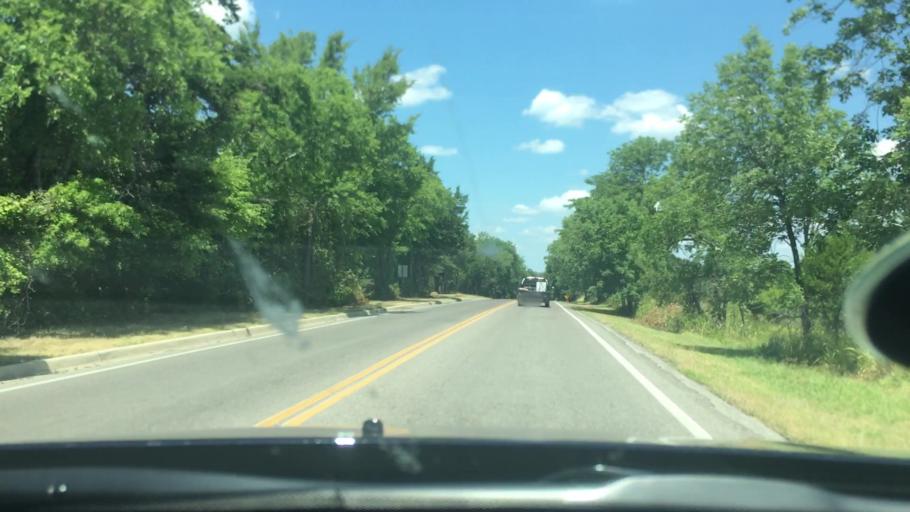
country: US
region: Oklahoma
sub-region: Murray County
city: Sulphur
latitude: 34.4963
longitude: -96.9694
